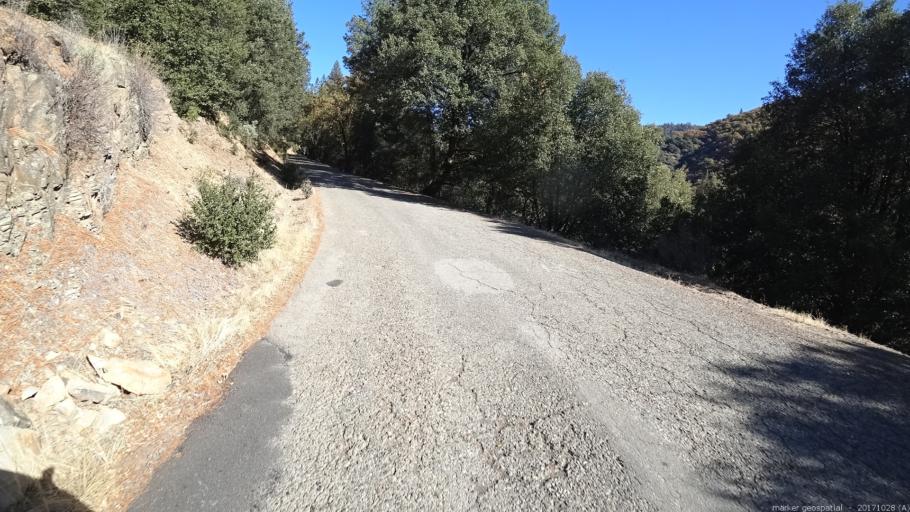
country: US
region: California
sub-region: Trinity County
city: Lewiston
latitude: 40.7929
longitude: -122.6120
